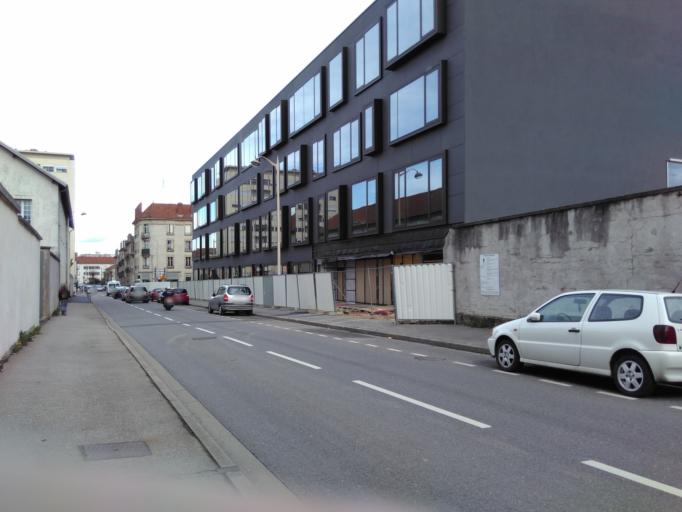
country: FR
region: Lorraine
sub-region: Departement de Meurthe-et-Moselle
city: Villers-les-Nancy
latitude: 48.6747
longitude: 6.1690
